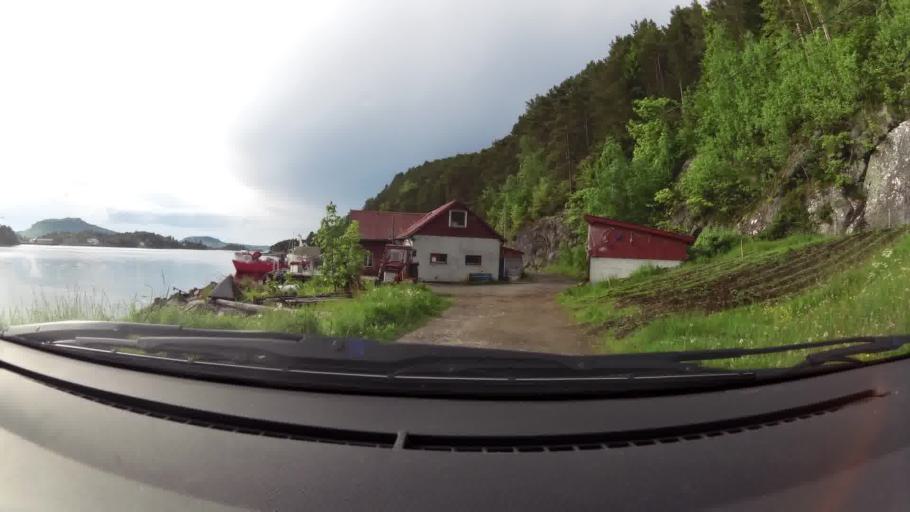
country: NO
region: More og Romsdal
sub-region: Kristiansund
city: Kristiansund
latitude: 63.0565
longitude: 7.7275
